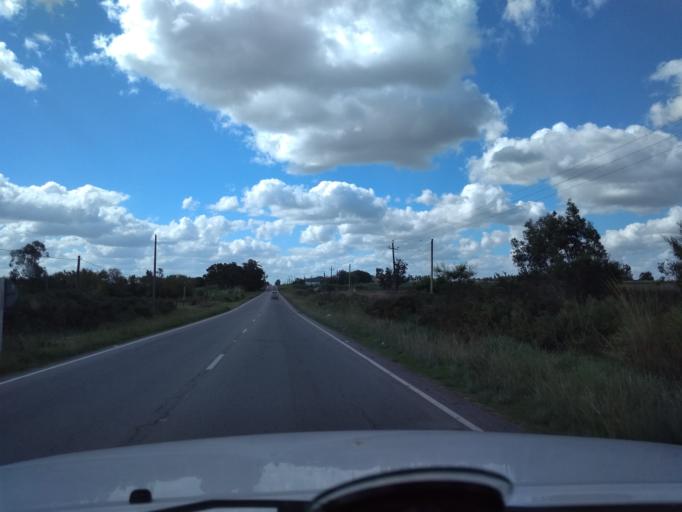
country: UY
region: Canelones
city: Joaquin Suarez
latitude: -34.6998
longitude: -56.0568
